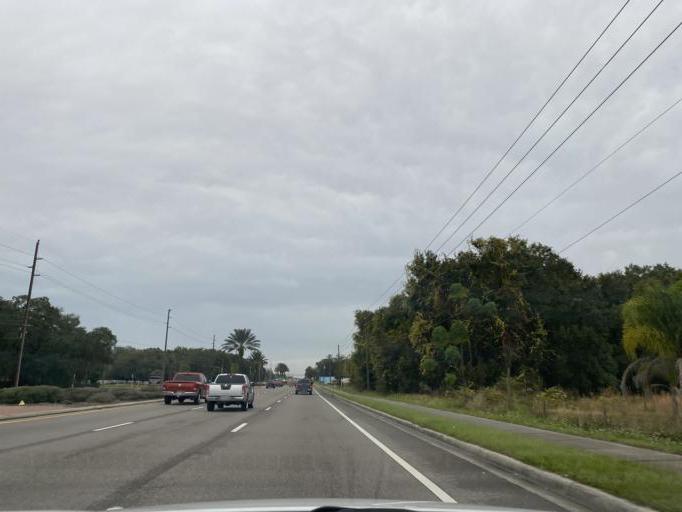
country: US
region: Florida
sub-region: Orange County
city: Winter Garden
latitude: 28.5512
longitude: -81.6019
